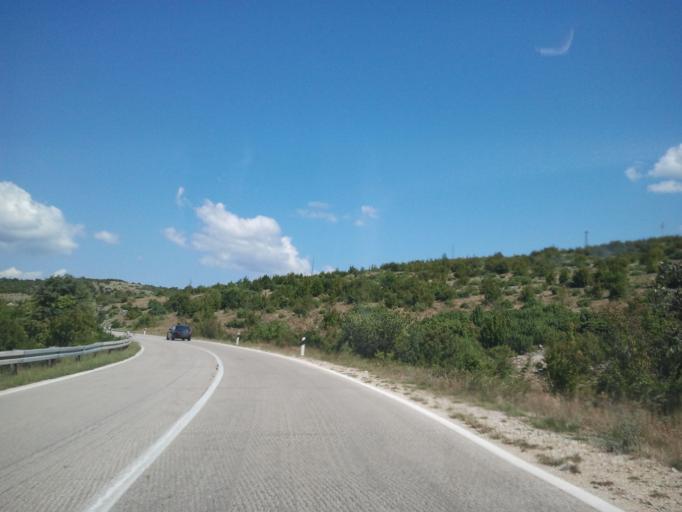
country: HR
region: Zadarska
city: Krusevo
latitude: 44.1808
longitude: 15.6205
